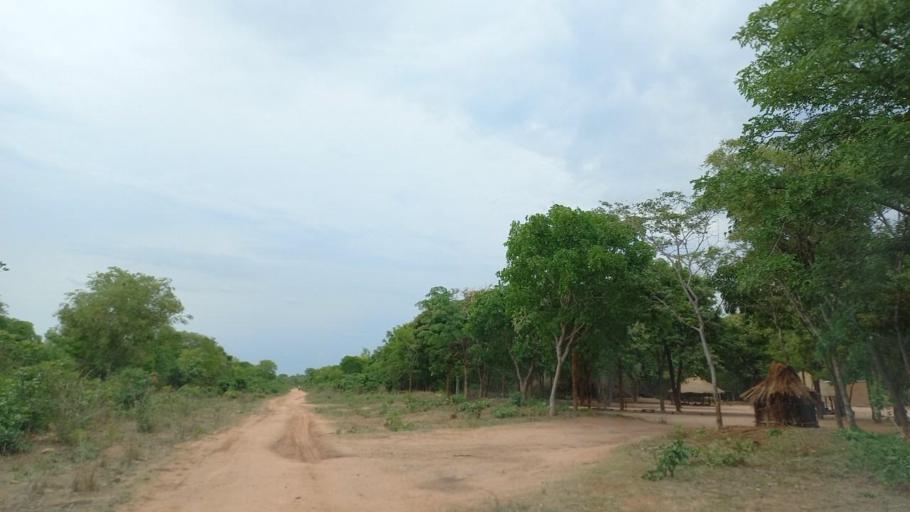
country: ZM
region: North-Western
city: Mufumbwe
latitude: -13.6485
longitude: 24.9793
